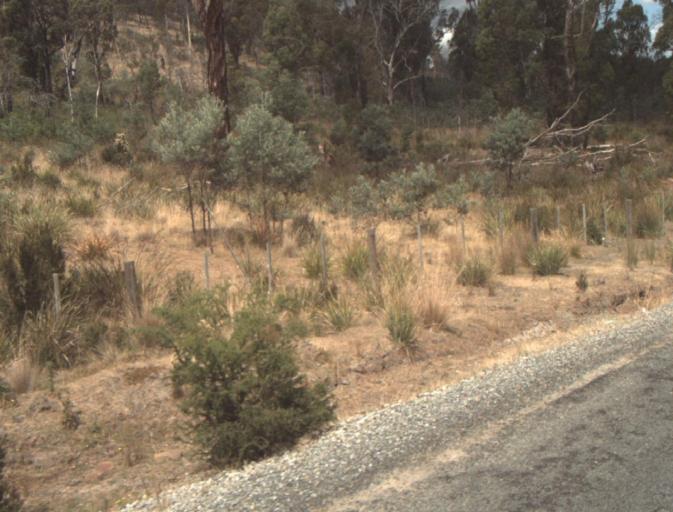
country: AU
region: Tasmania
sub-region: Launceston
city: Mayfield
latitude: -41.2931
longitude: 147.0479
